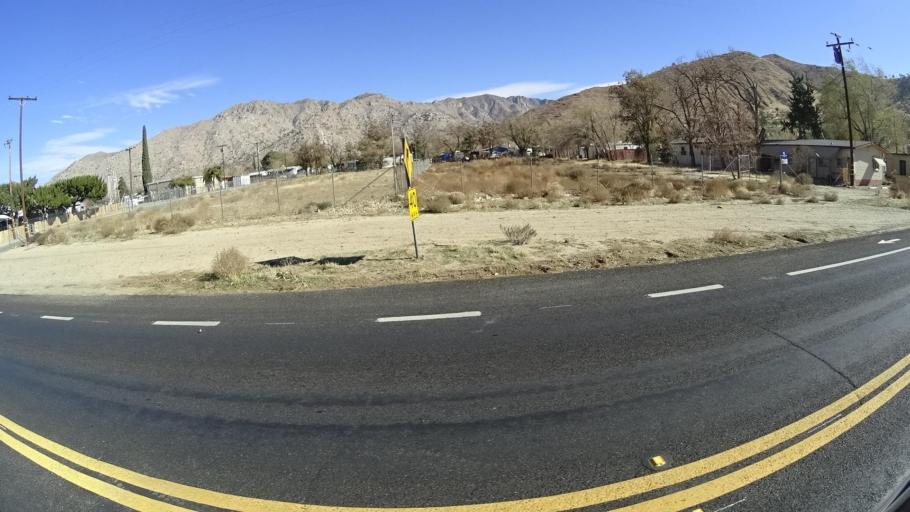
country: US
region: California
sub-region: Kern County
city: Bodfish
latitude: 35.6034
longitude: -118.4862
